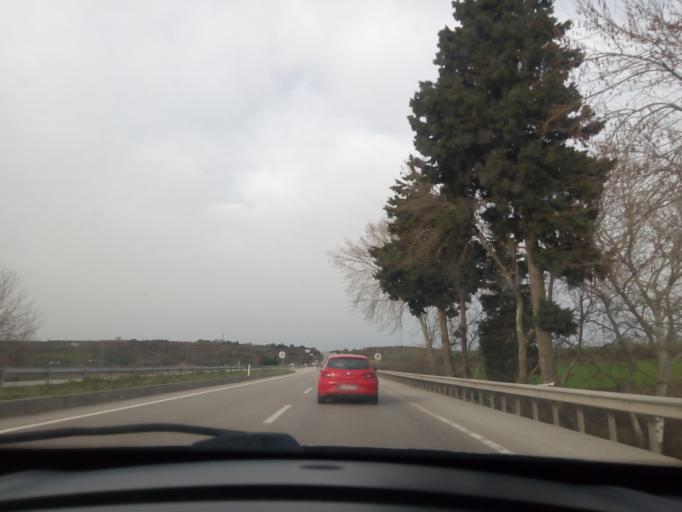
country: TR
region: Bursa
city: Mahmudiye
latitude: 40.2167
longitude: 28.6517
